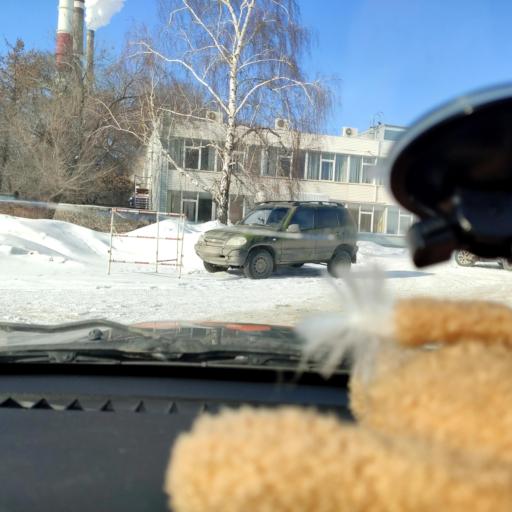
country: RU
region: Samara
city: Tol'yatti
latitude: 53.5741
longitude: 49.2534
